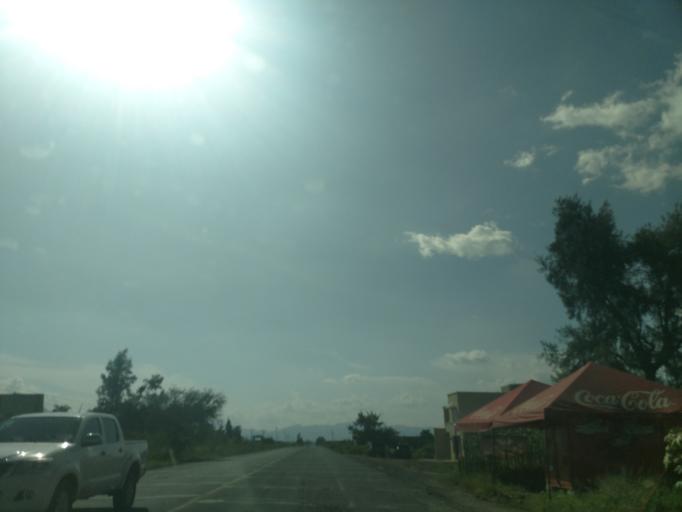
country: MX
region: Jalisco
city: Teuchitlan
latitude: 20.6817
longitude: -103.8531
